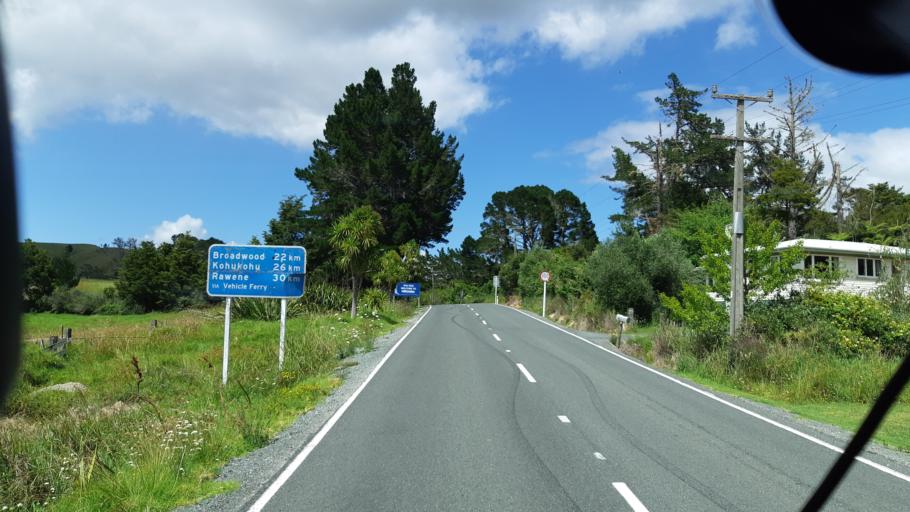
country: NZ
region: Northland
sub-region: Far North District
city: Taipa
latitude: -35.2373
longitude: 173.5432
